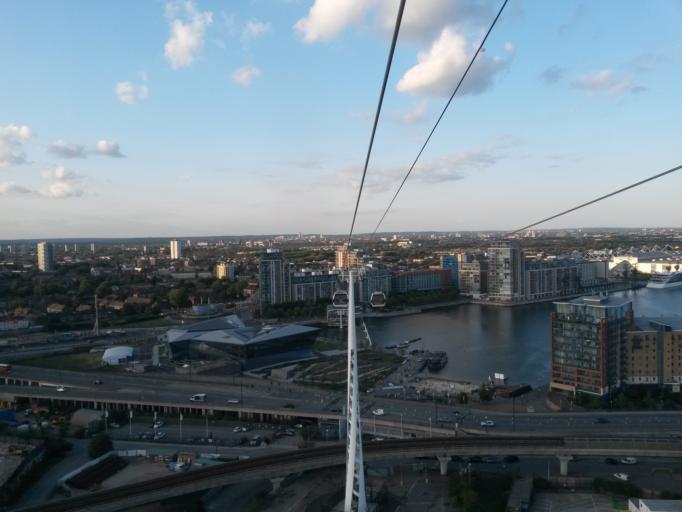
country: GB
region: England
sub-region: Greater London
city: Poplar
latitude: 51.5047
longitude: 0.0143
